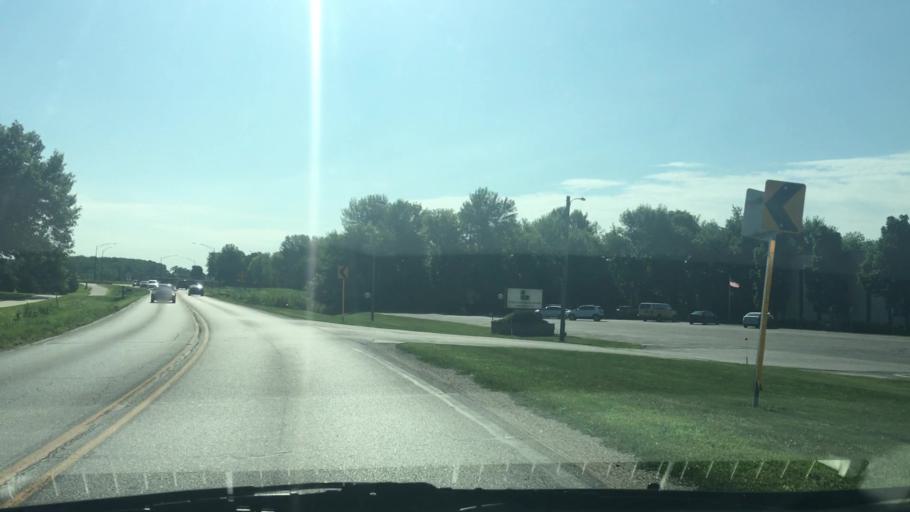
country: US
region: Iowa
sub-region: Johnson County
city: North Liberty
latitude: 41.7337
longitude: -91.5790
